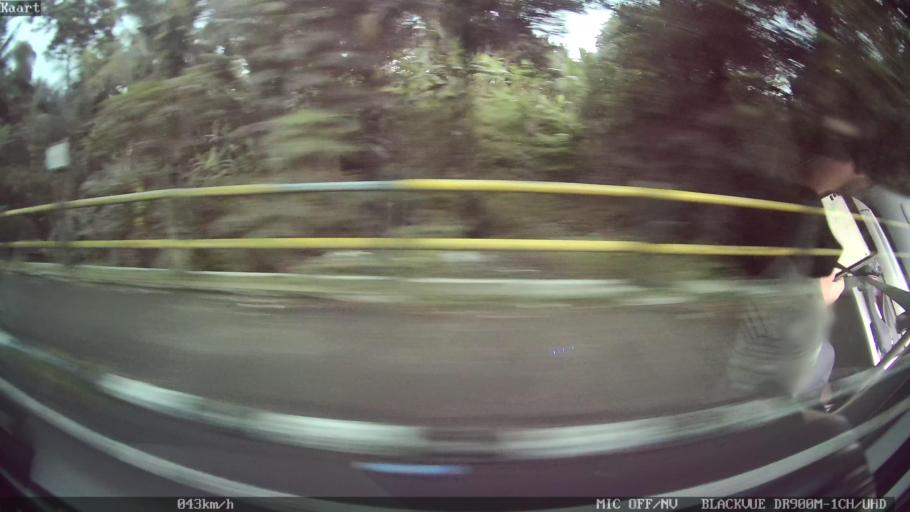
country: ID
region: Bali
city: Banjar Sempidi
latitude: -8.5231
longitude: 115.1971
